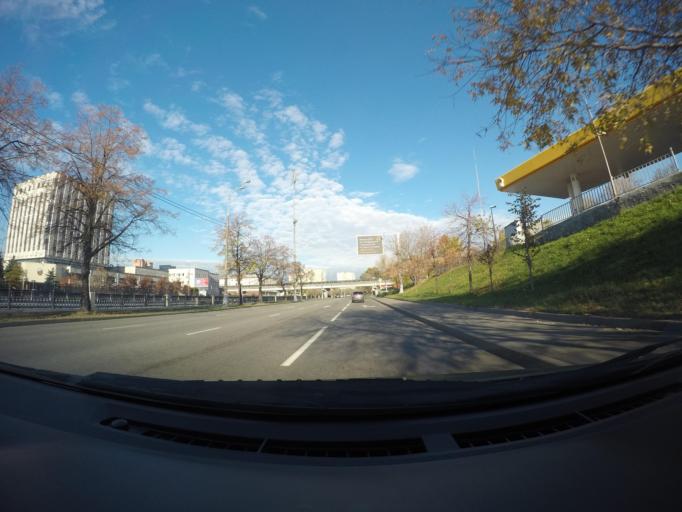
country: RU
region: Moskovskaya
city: Bogorodskoye
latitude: 55.7956
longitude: 37.7036
